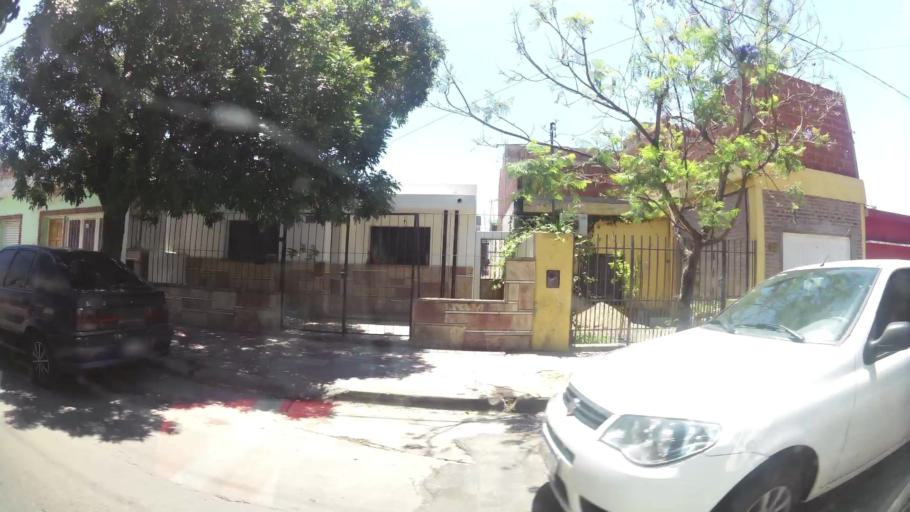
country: AR
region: Cordoba
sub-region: Departamento de Capital
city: Cordoba
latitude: -31.3953
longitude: -64.2068
